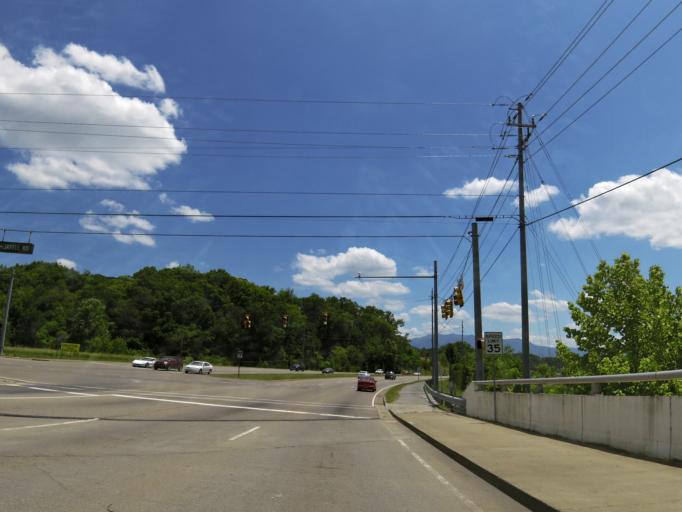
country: US
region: Tennessee
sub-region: Sevier County
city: Pigeon Forge
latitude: 35.8171
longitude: -83.5392
